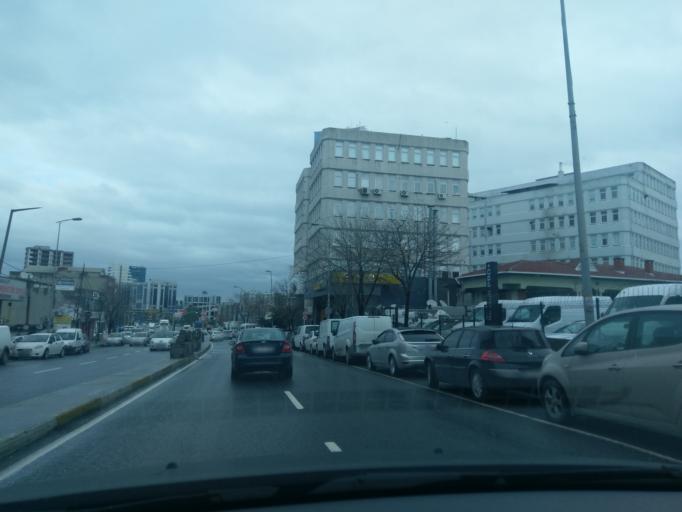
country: TR
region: Istanbul
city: Mahmutbey
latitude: 41.0610
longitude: 28.8323
